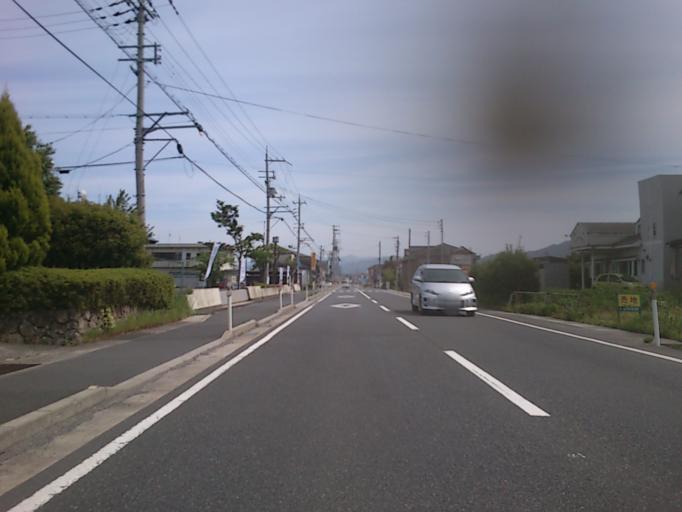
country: JP
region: Kyoto
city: Miyazu
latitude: 35.6265
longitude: 135.0725
